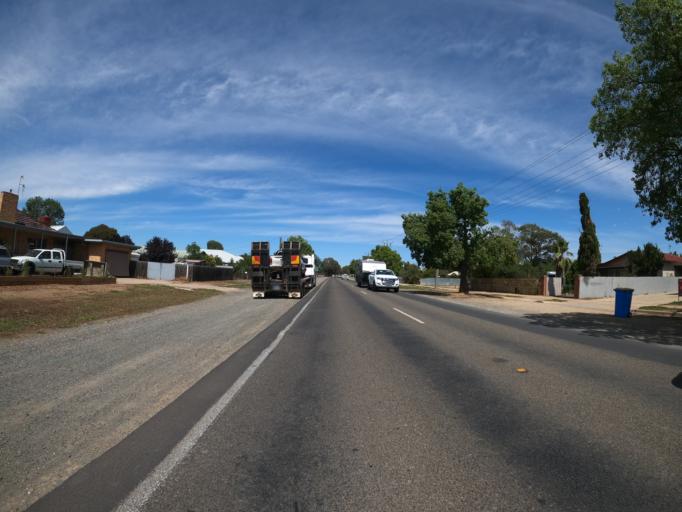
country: AU
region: Victoria
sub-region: Moira
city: Yarrawonga
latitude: -36.0198
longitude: 145.9976
